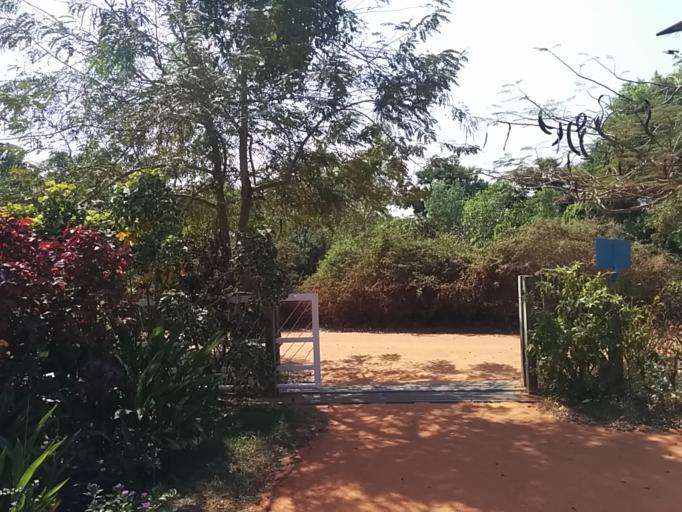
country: IN
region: Tamil Nadu
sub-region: Villupuram
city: Auroville
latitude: 12.0064
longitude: 79.8039
